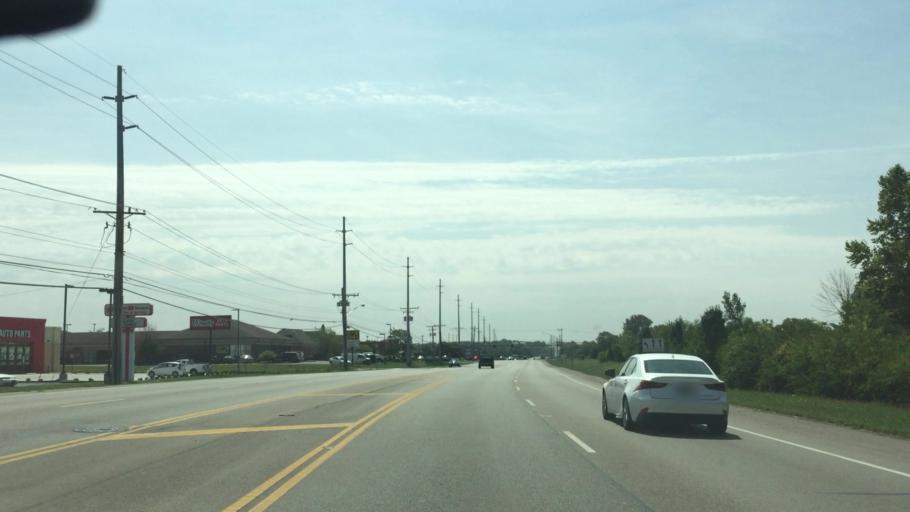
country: US
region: Ohio
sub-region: Butler County
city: Beckett Ridge
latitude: 39.3464
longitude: -84.4614
